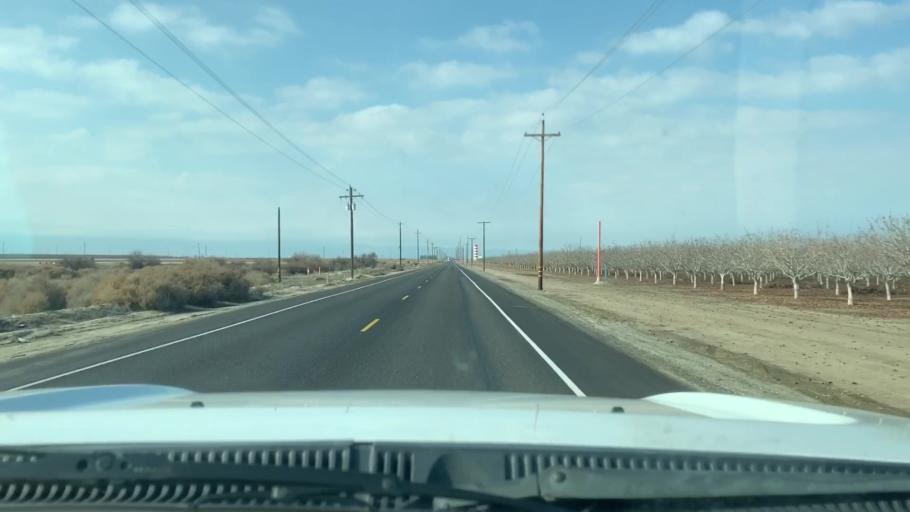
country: US
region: California
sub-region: Kern County
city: Buttonwillow
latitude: 35.4423
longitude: -119.4334
